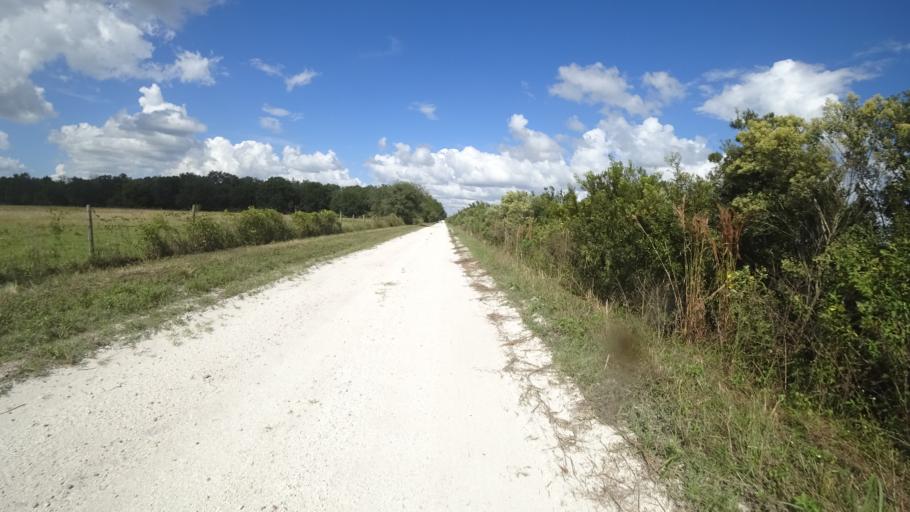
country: US
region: Florida
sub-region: DeSoto County
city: Arcadia
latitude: 27.3308
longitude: -82.1050
